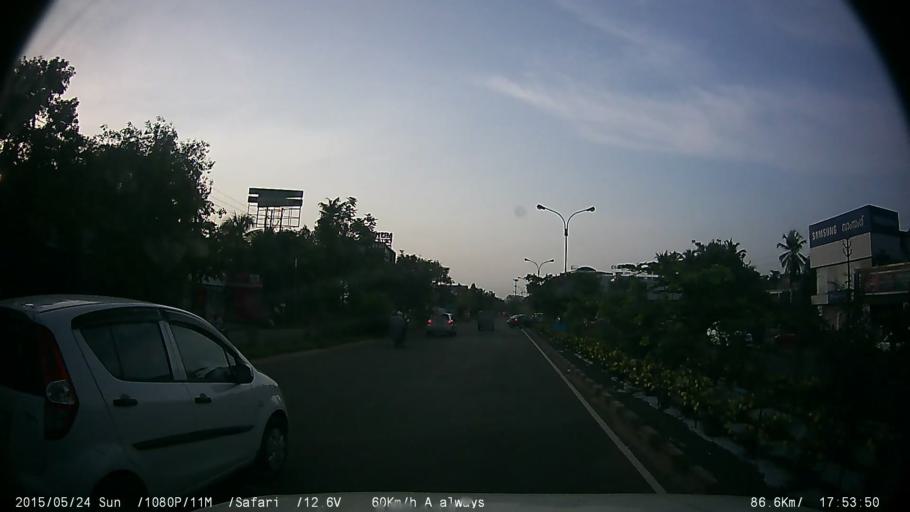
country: IN
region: Kerala
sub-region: Ernakulam
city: Elur
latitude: 10.0115
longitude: 76.3119
